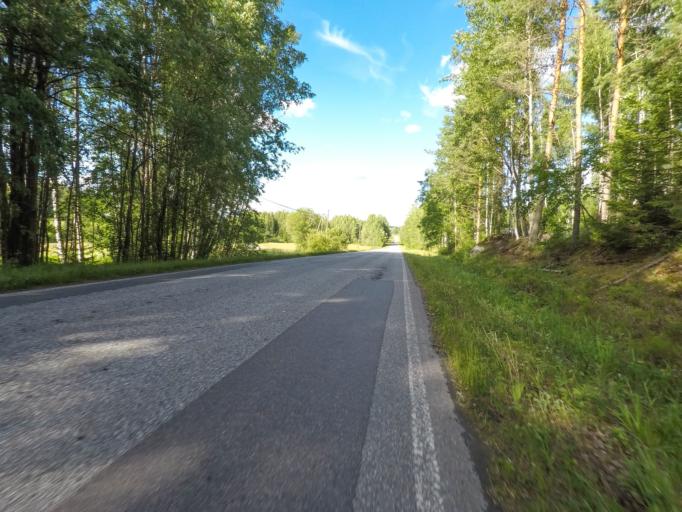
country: FI
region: South Karelia
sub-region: Imatra
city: Imatra
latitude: 61.1331
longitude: 28.7285
